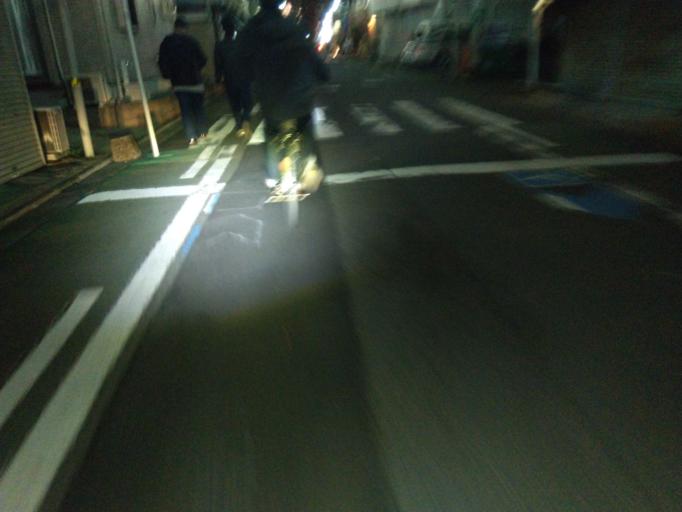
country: JP
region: Kanagawa
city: Hiratsuka
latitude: 35.3333
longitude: 139.3507
